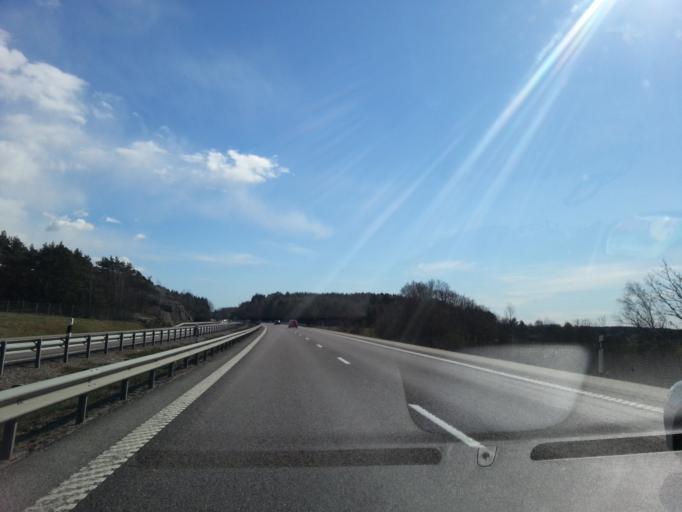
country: SE
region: Vaestra Goetaland
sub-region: Stenungsunds Kommun
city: Stora Hoga
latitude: 57.9976
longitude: 11.8428
